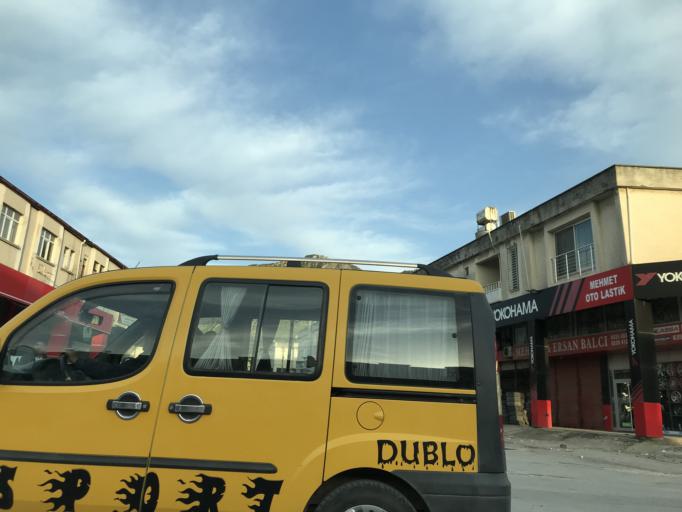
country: TR
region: Hatay
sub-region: Antakya Ilcesi
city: Antakya
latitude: 36.2097
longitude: 36.1657
